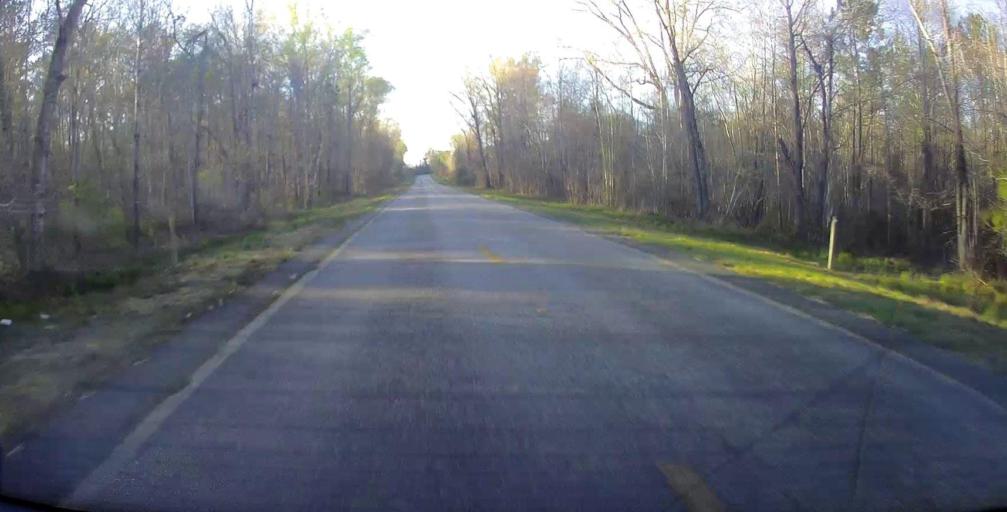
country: US
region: Georgia
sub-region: Wilcox County
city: Abbeville
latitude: 32.0994
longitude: -83.3030
